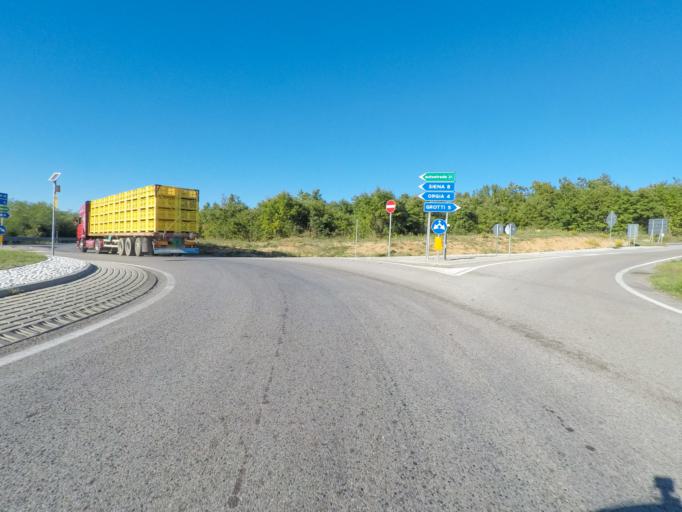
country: IT
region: Tuscany
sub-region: Provincia di Siena
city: Rosia
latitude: 43.2195
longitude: 11.2750
